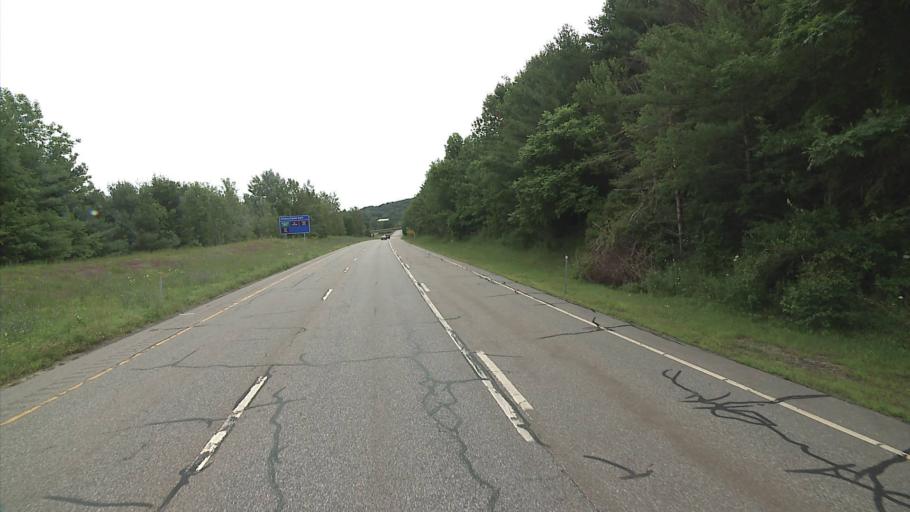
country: US
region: Connecticut
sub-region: Litchfield County
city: Winsted
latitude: 41.9049
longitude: -73.0640
